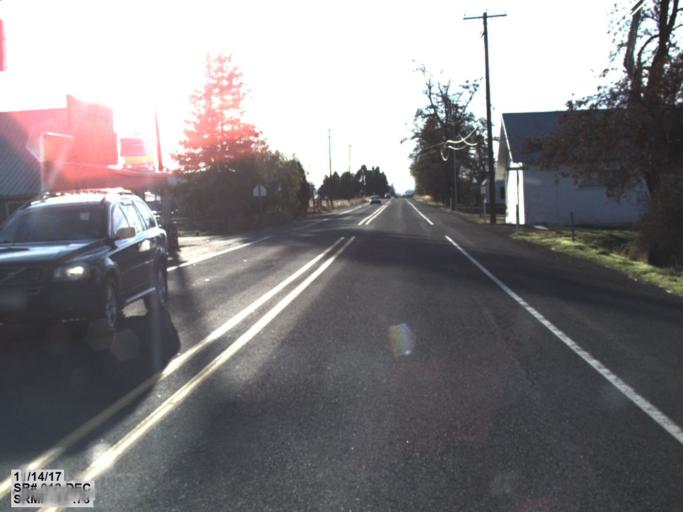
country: US
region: Washington
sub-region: Walla Walla County
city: Waitsburg
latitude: 46.1398
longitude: -118.1561
